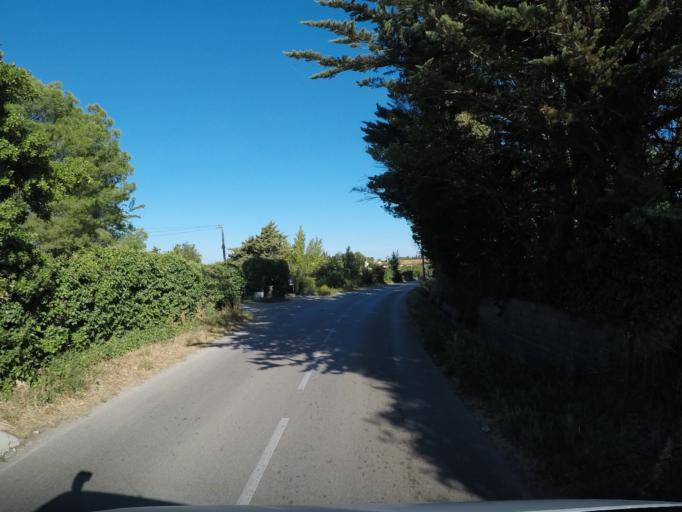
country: FR
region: Languedoc-Roussillon
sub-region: Departement de l'Aude
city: Narbonne
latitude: 43.1658
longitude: 3.0102
